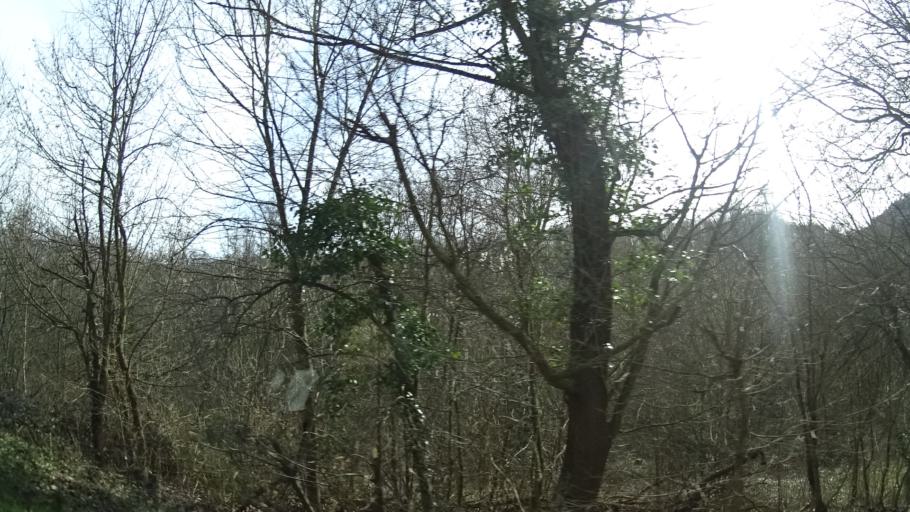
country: DE
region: Rheinland-Pfalz
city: Rhodt unter Rietburg
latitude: 49.2830
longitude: 8.0912
